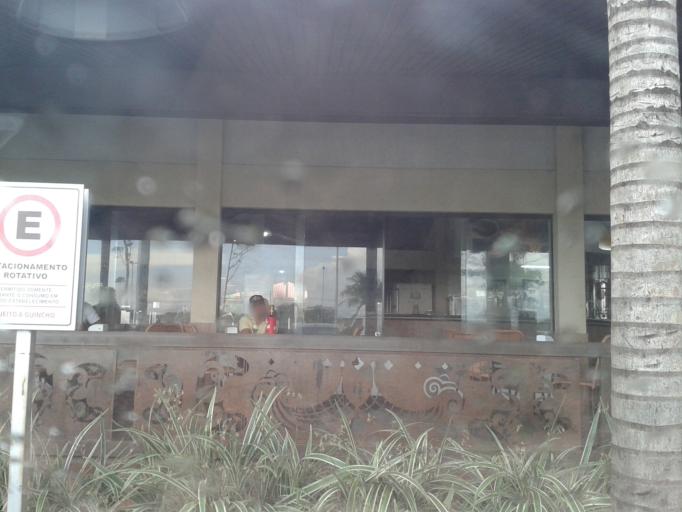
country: BR
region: Minas Gerais
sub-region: Ituiutaba
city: Ituiutaba
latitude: -18.9651
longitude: -49.5007
